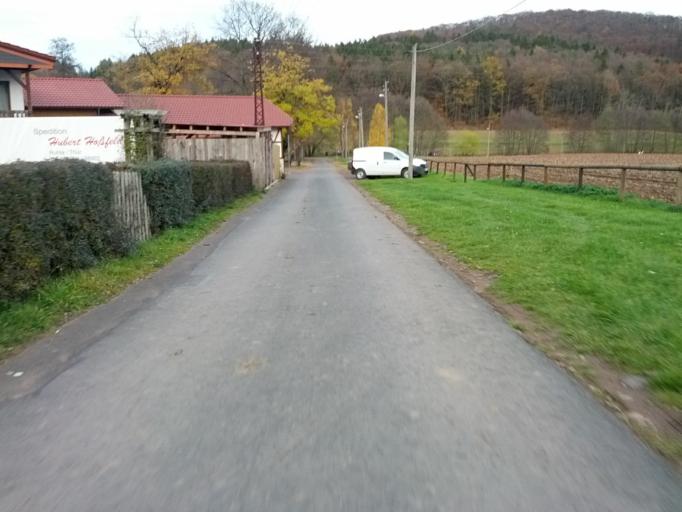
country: DE
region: Thuringia
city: Eisenach
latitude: 50.9394
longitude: 10.3424
